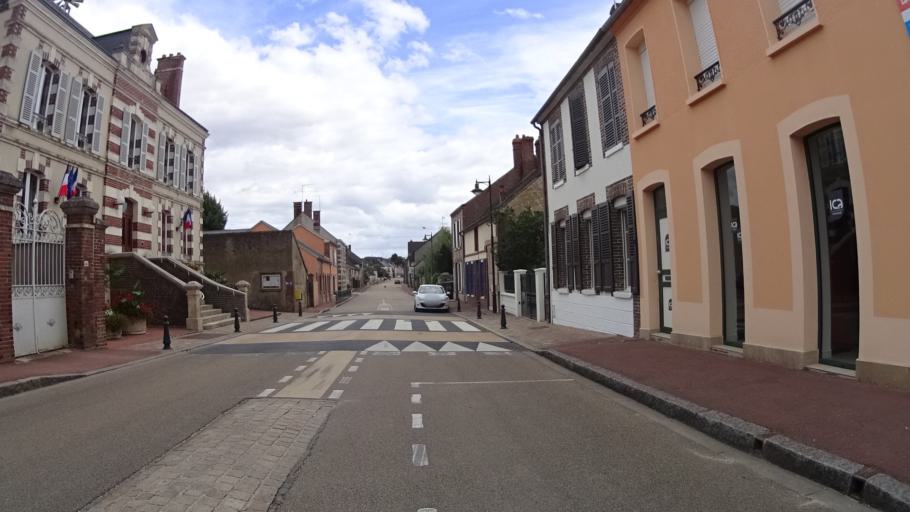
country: FR
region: Centre
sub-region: Departement du Loiret
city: Douchy
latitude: 47.9434
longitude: 3.0503
